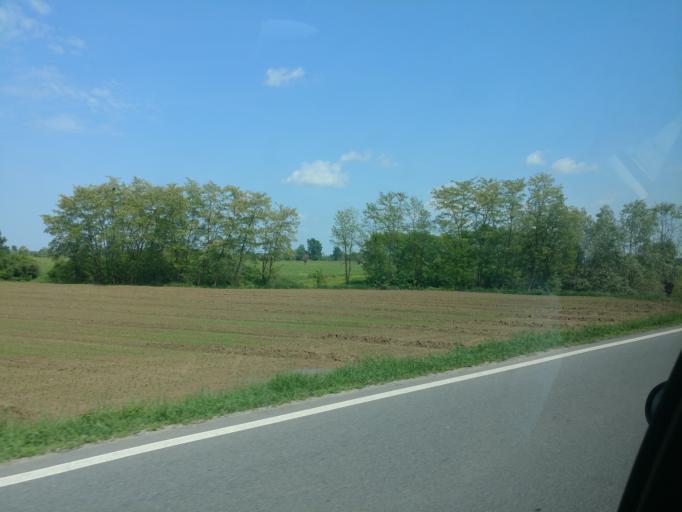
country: IT
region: Piedmont
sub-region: Provincia di Cuneo
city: Carde
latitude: 44.7258
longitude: 7.4336
